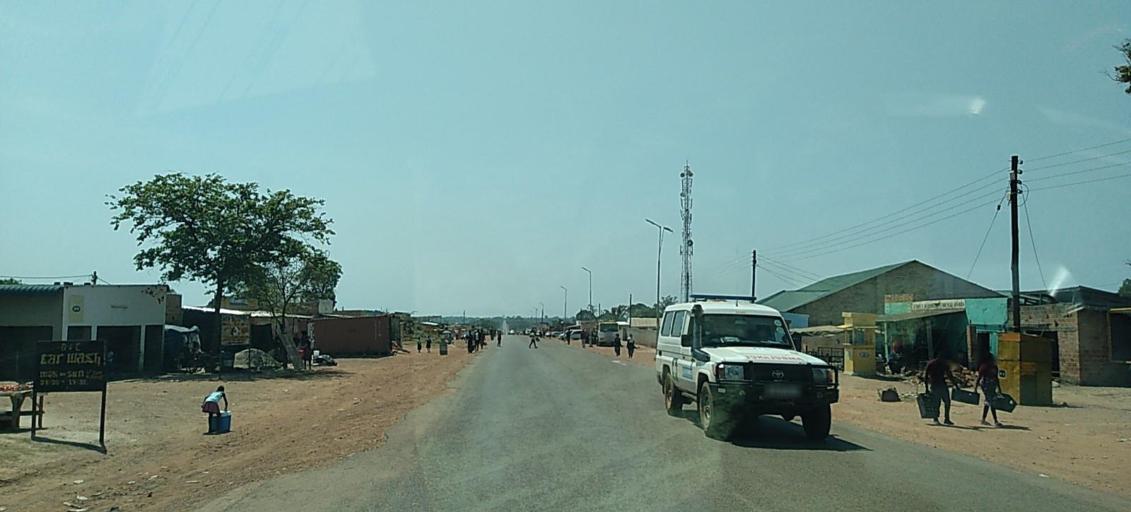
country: ZM
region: North-Western
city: Solwezi
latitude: -12.3124
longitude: 25.8474
